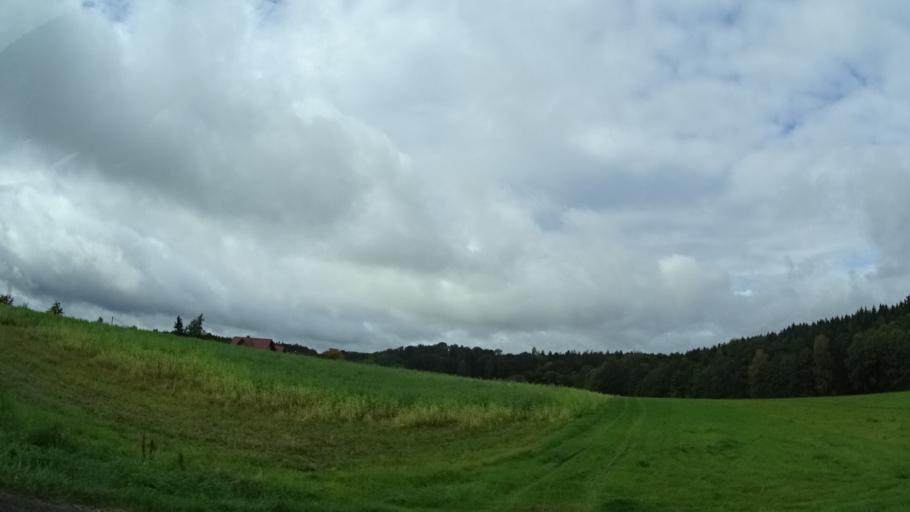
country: DE
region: Bavaria
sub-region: Upper Franconia
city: Zapfendorf
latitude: 50.0025
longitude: 10.9727
